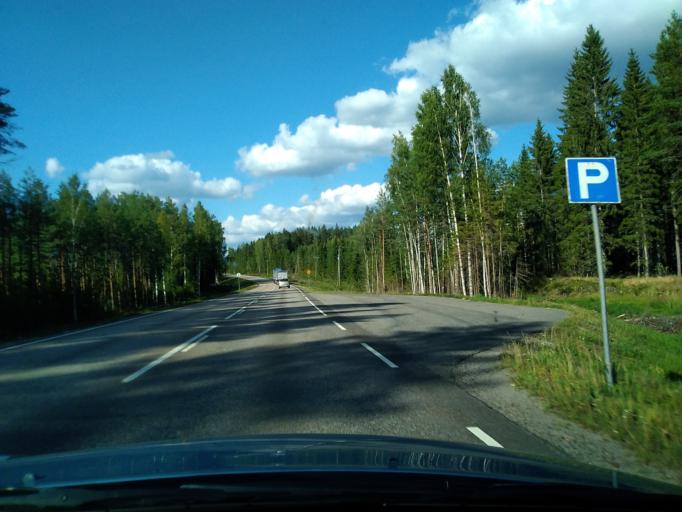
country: FI
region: Pirkanmaa
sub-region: Ylae-Pirkanmaa
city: Maenttae
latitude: 62.0731
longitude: 24.7233
